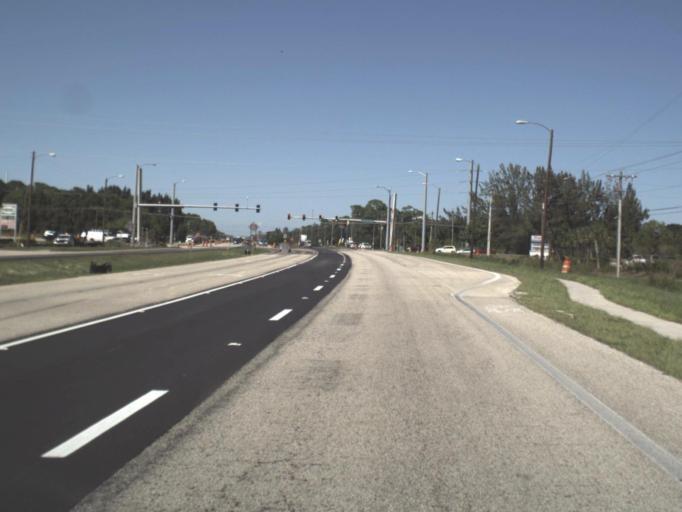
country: US
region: Florida
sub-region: Lee County
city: Palmona Park
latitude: 26.7238
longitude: -81.9059
